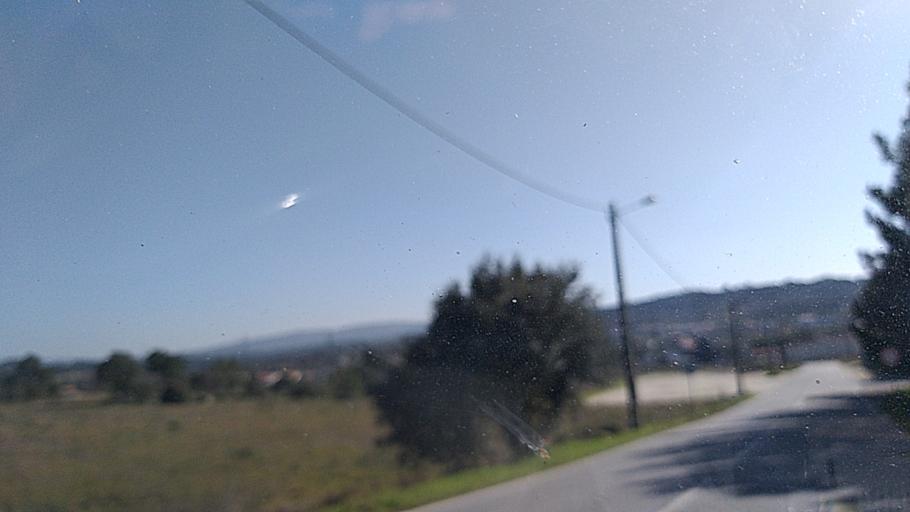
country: PT
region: Guarda
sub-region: Celorico da Beira
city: Celorico da Beira
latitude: 40.6703
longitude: -7.3883
